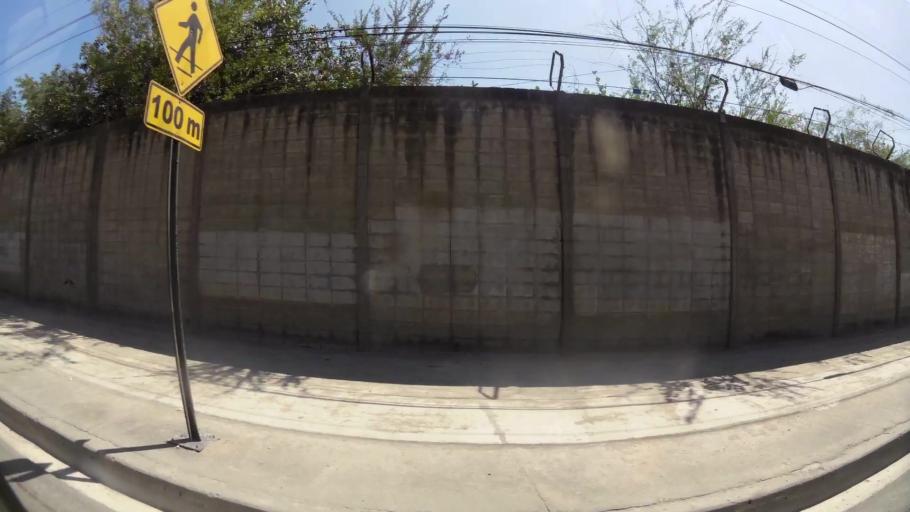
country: EC
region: Guayas
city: Guayaquil
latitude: -2.1932
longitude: -79.9359
